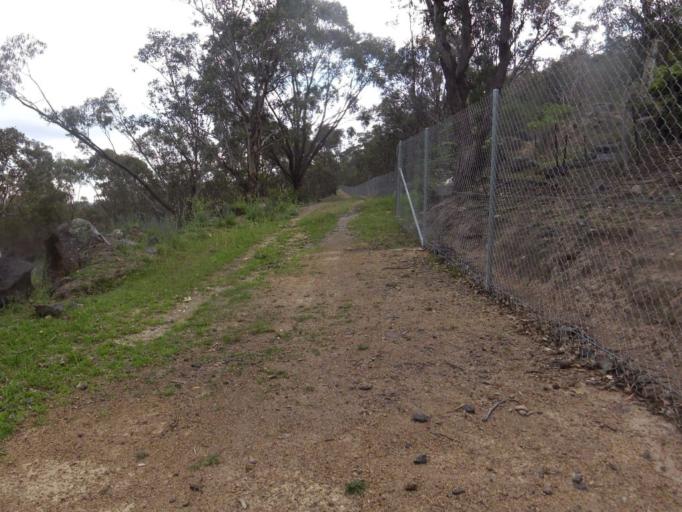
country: AU
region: Australian Capital Territory
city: Forrest
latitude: -35.3543
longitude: 149.1245
